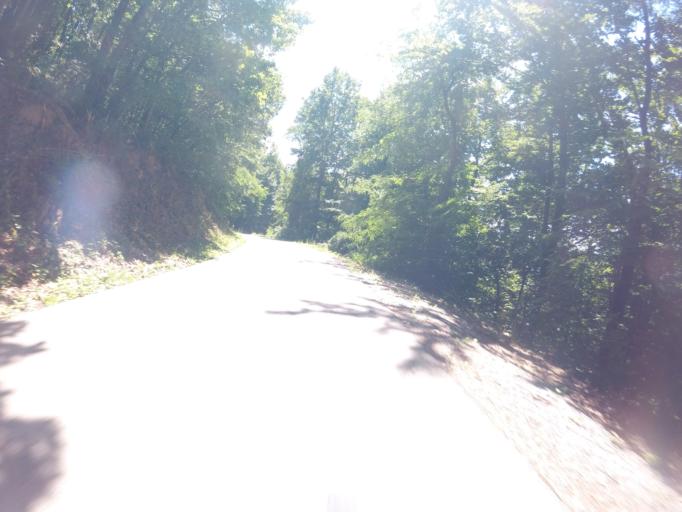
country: HR
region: Karlovacka
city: Ozalj
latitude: 45.6867
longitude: 15.4111
